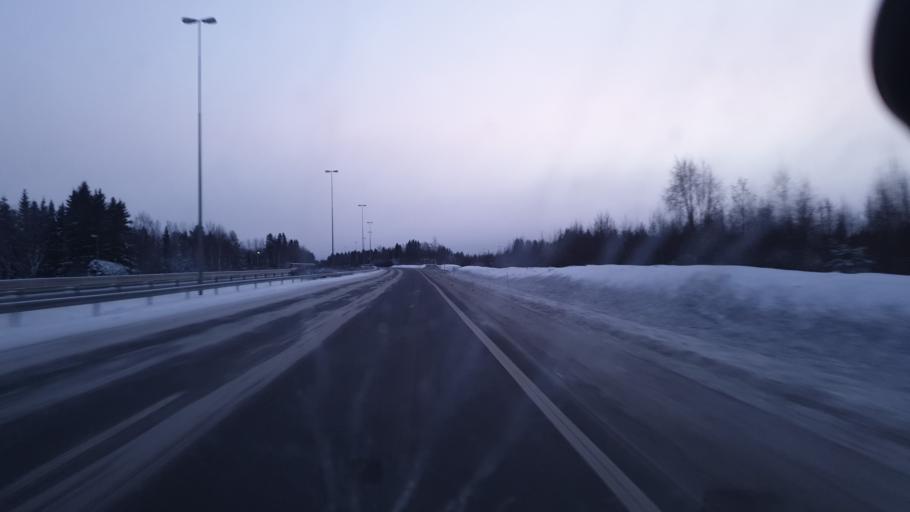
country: FI
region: Lapland
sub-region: Kemi-Tornio
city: Tornio
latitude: 65.8386
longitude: 24.2189
